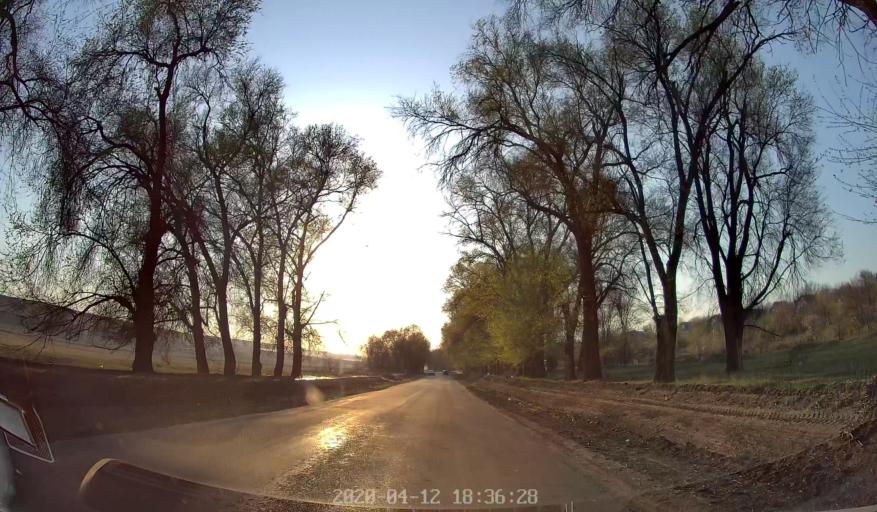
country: MD
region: Chisinau
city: Vadul lui Voda
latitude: 47.1169
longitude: 29.0297
